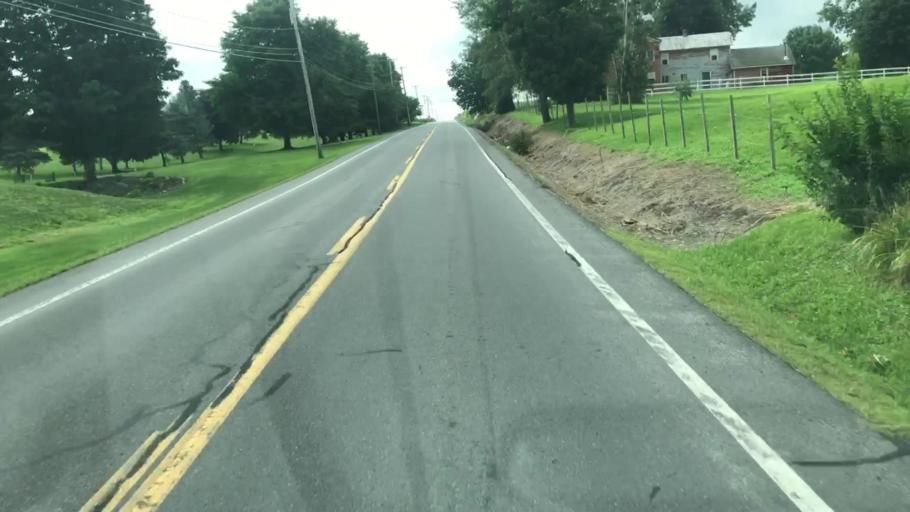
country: US
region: New York
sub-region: Onondaga County
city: Peru
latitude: 43.0461
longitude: -76.3660
